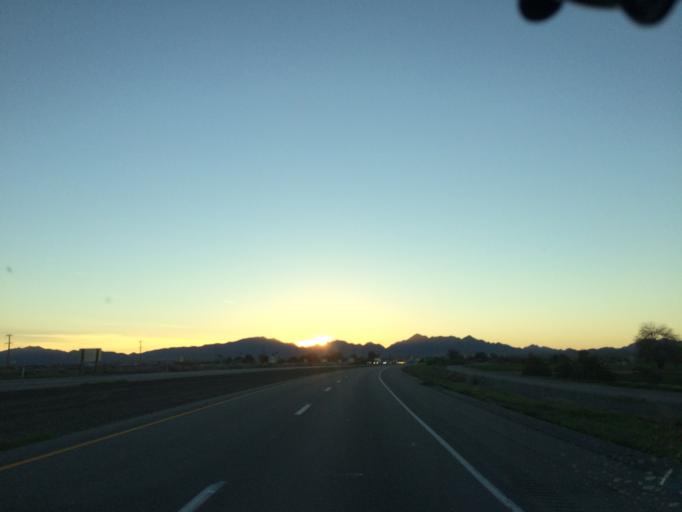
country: US
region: Arizona
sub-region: La Paz County
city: Ehrenberg
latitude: 33.6076
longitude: -114.5445
